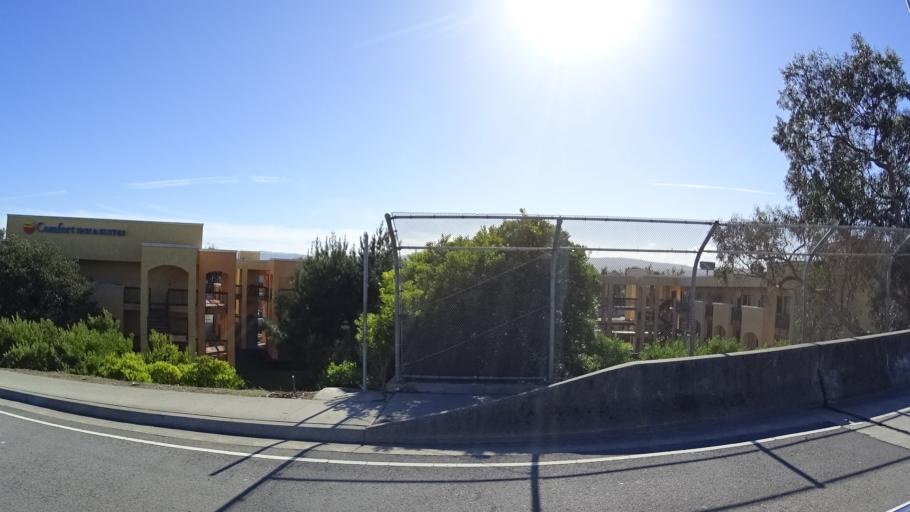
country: US
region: California
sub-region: San Mateo County
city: South San Francisco
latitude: 37.6554
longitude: -122.4044
